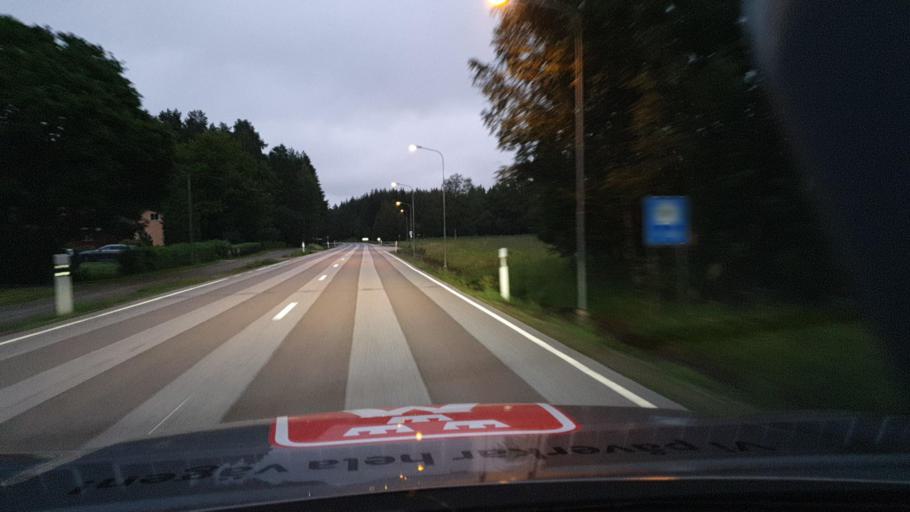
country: SE
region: OErebro
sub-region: Hallefors Kommun
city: Haellefors
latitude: 59.7412
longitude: 14.4865
